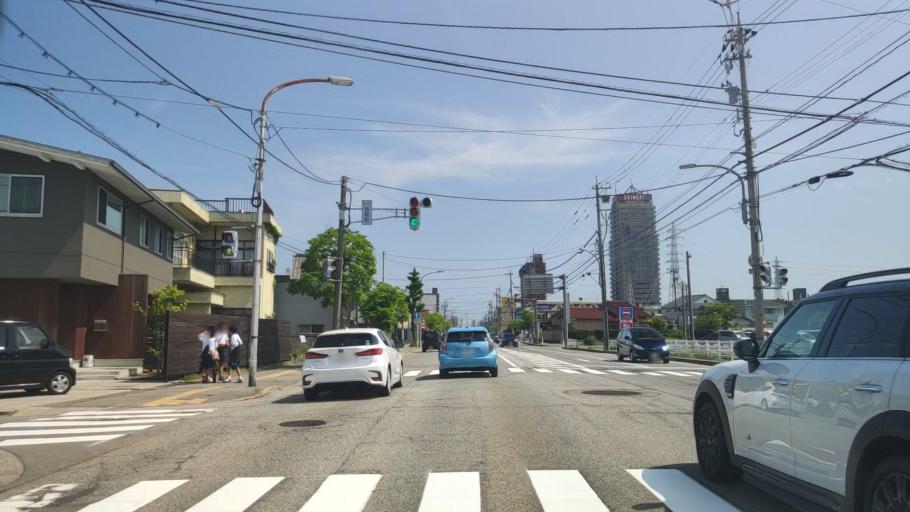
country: JP
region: Toyama
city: Toyama-shi
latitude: 36.7038
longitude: 137.2283
